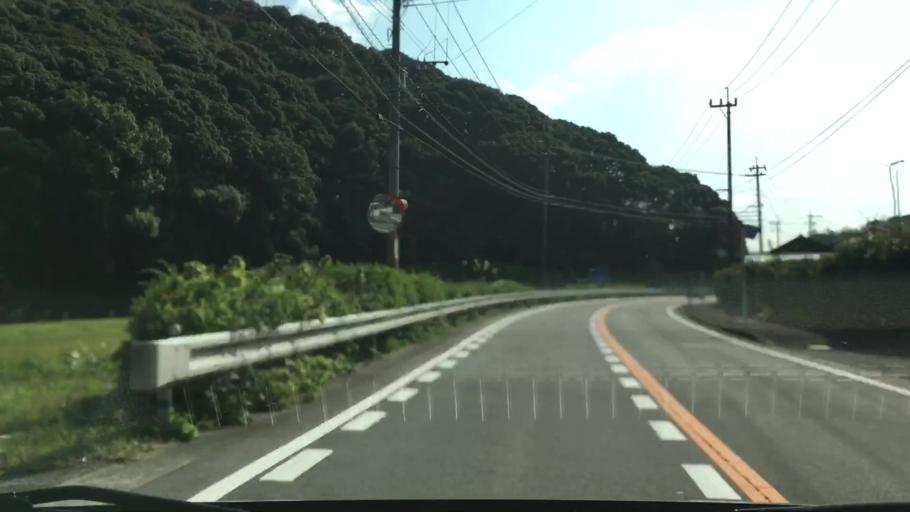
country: JP
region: Nagasaki
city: Togitsu
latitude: 32.9540
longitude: 129.7855
